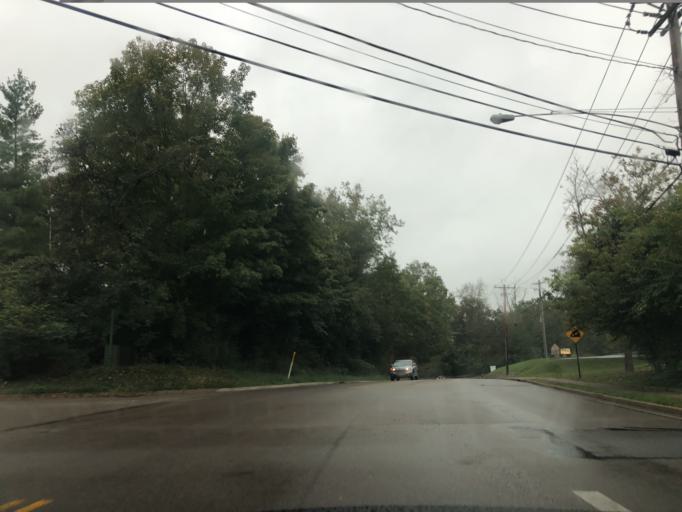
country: US
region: Ohio
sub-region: Hamilton County
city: The Village of Indian Hill
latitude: 39.2607
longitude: -84.2868
